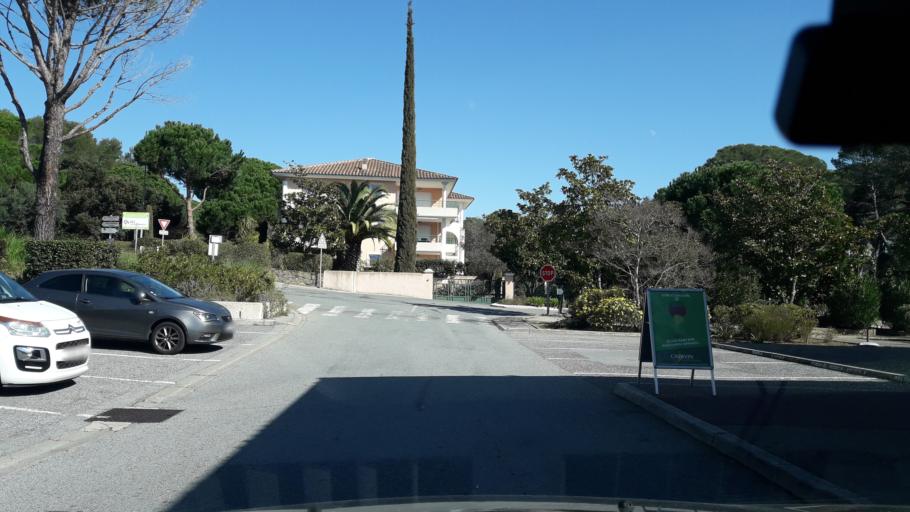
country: FR
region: Provence-Alpes-Cote d'Azur
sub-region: Departement du Var
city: Saint-Raphael
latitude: 43.4529
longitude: 6.7833
